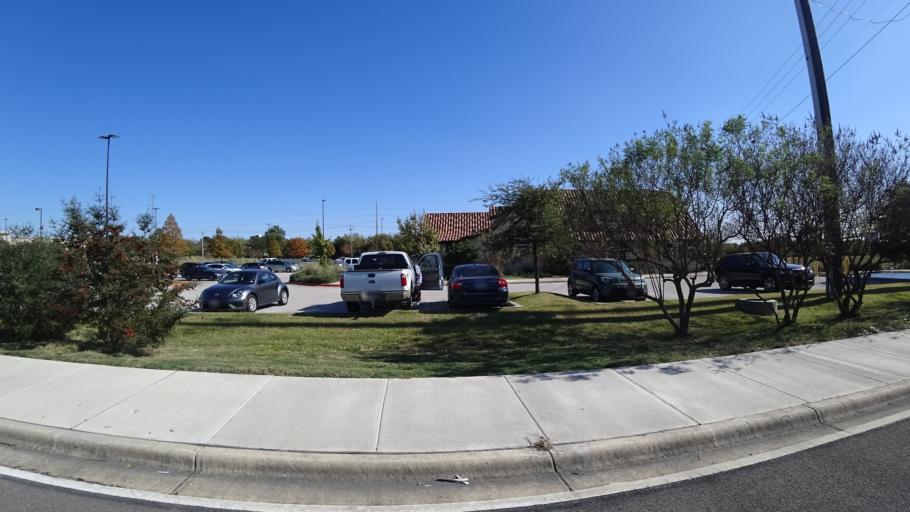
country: US
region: Texas
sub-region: Williamson County
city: Jollyville
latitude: 30.3860
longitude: -97.7347
